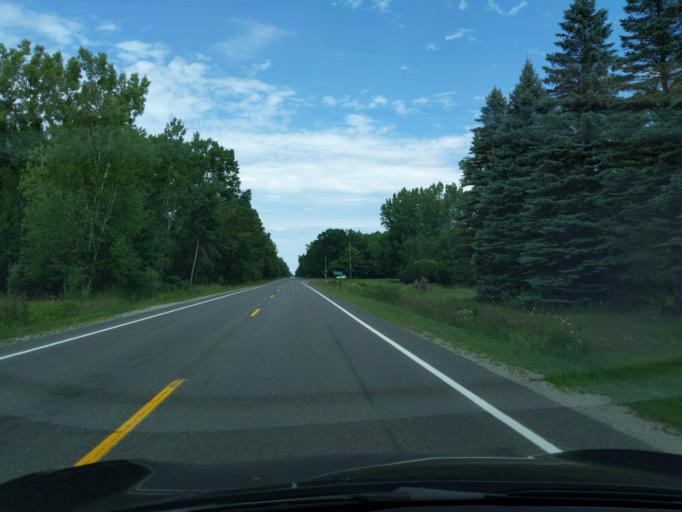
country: US
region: Michigan
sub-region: Midland County
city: Midland
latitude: 43.5235
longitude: -84.3699
